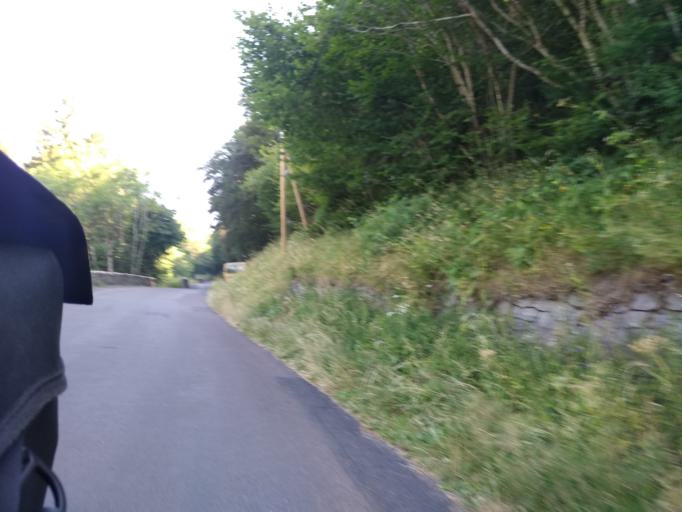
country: FR
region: Auvergne
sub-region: Departement du Puy-de-Dome
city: Mont-Dore
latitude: 45.5696
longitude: 2.8150
